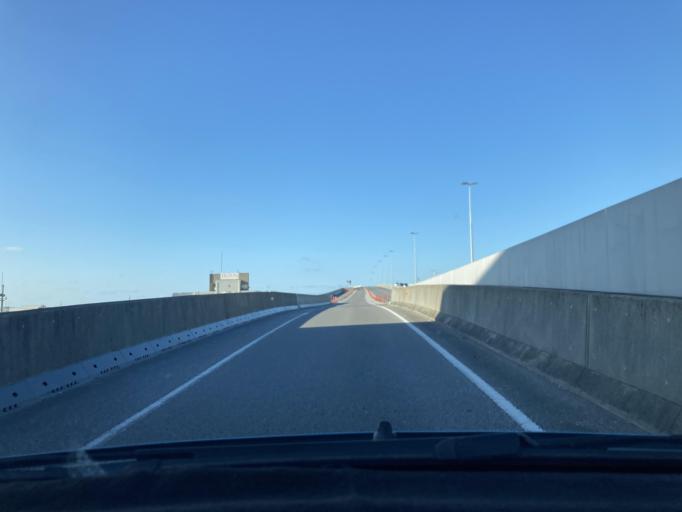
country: JP
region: Okinawa
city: Itoman
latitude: 26.1290
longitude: 127.6654
